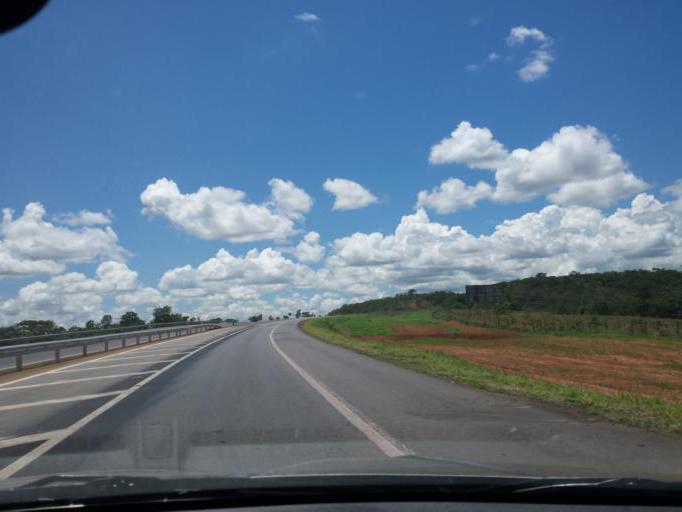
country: BR
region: Goias
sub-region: Cristalina
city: Cristalina
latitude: -16.6288
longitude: -47.7401
